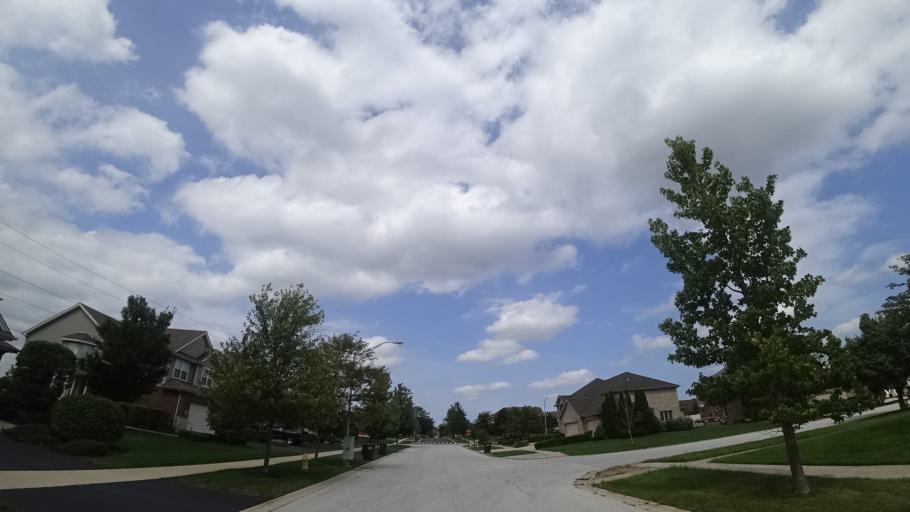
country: US
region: Illinois
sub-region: Cook County
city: Tinley Park
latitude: 41.5647
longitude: -87.8167
